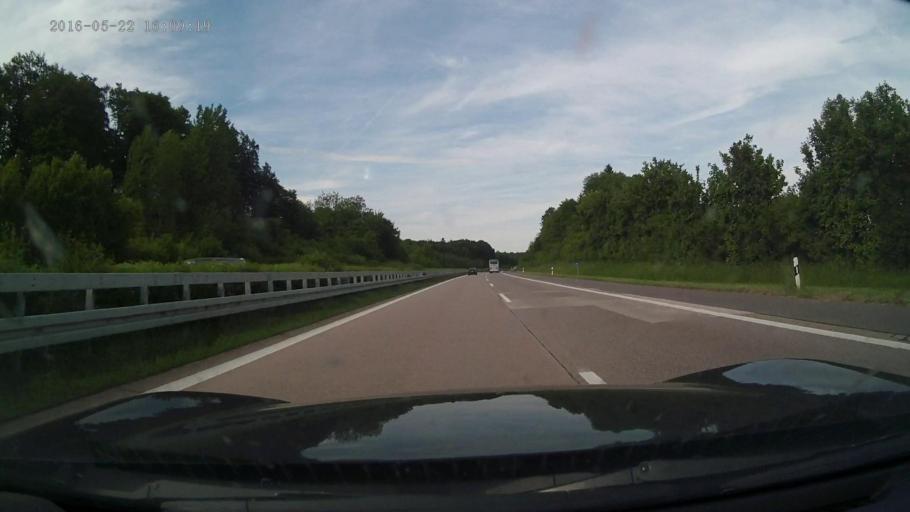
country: DE
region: Baden-Wuerttemberg
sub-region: Regierungsbezirk Stuttgart
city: Widdern
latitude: 49.3497
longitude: 9.4095
